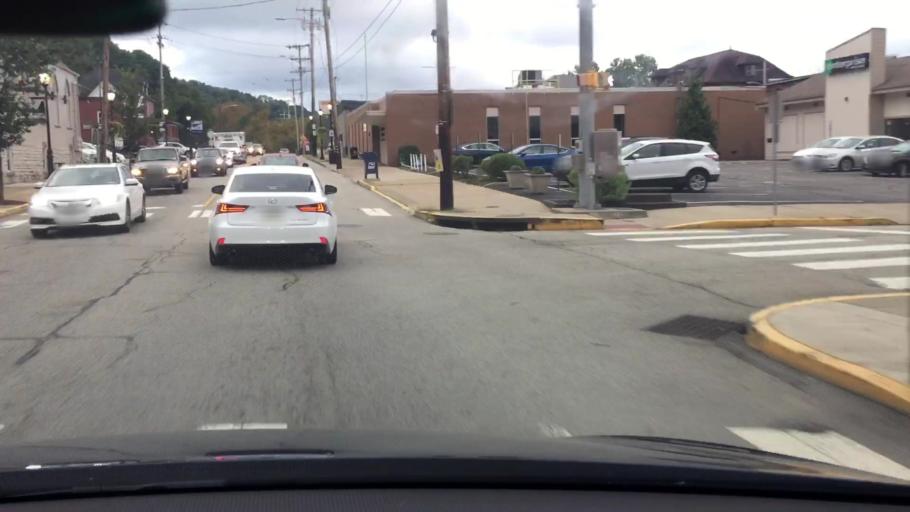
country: US
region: Pennsylvania
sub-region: Allegheny County
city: Verona
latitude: 40.5062
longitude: -79.8429
